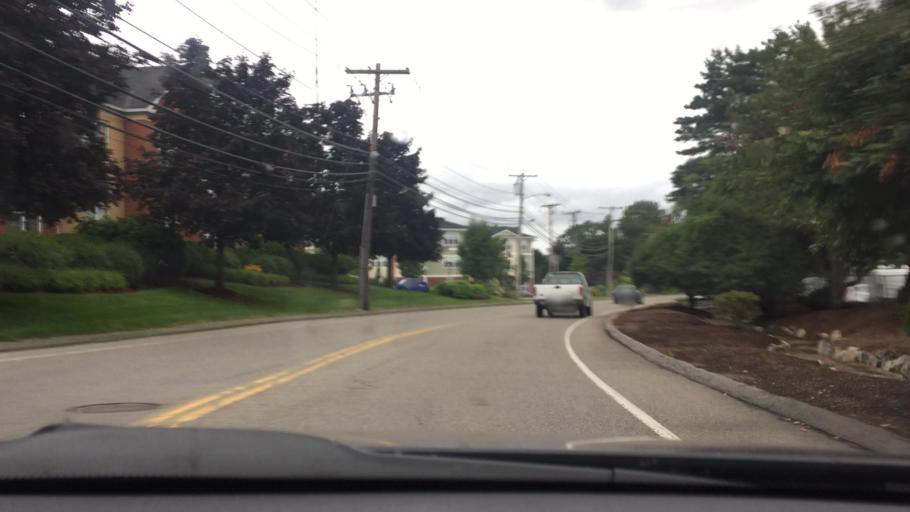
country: US
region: Massachusetts
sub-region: Norfolk County
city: Needham
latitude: 42.3009
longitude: -71.2295
